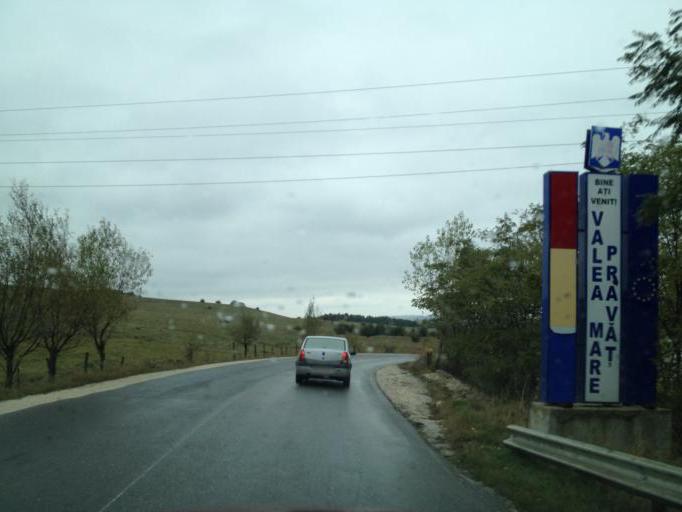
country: RO
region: Arges
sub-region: Comuna Valea Mare-Pravat
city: Valea Mare Pravat
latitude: 45.2934
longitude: 25.1200
